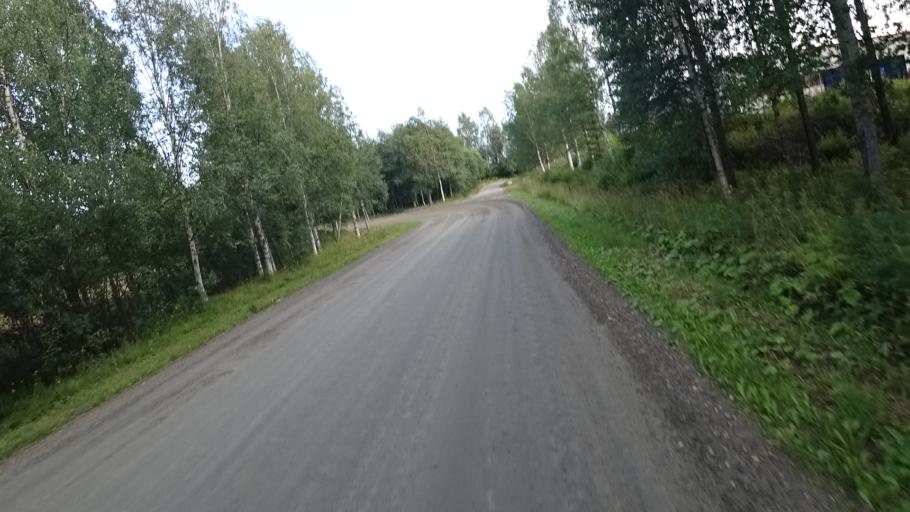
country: FI
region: North Karelia
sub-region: Joensuu
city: Ilomantsi
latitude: 62.6702
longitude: 30.9477
